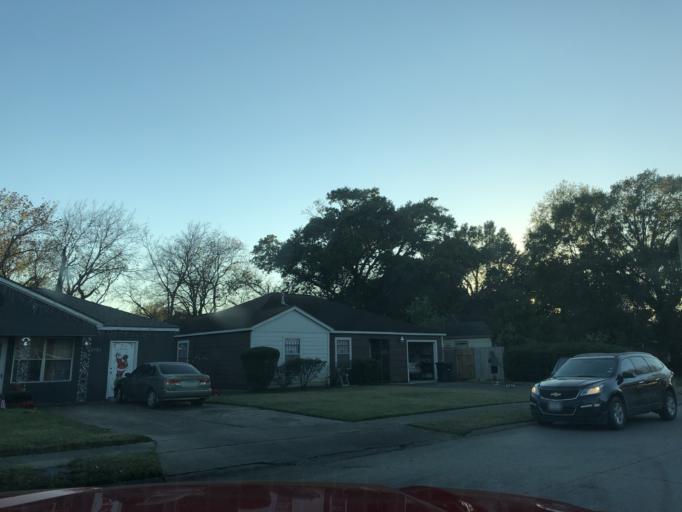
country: US
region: Texas
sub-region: Harris County
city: Jacinto City
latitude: 29.7627
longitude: -95.2662
